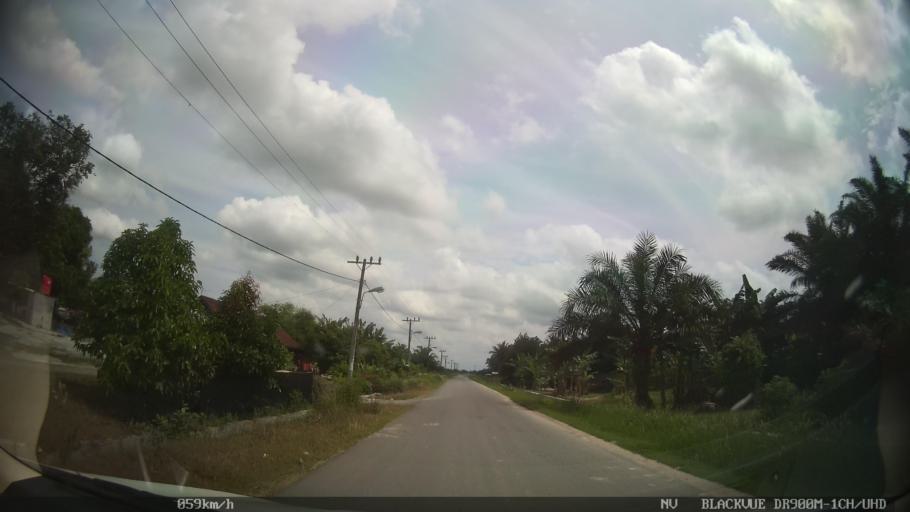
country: ID
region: North Sumatra
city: Percut
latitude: 3.5922
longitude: 98.8407
